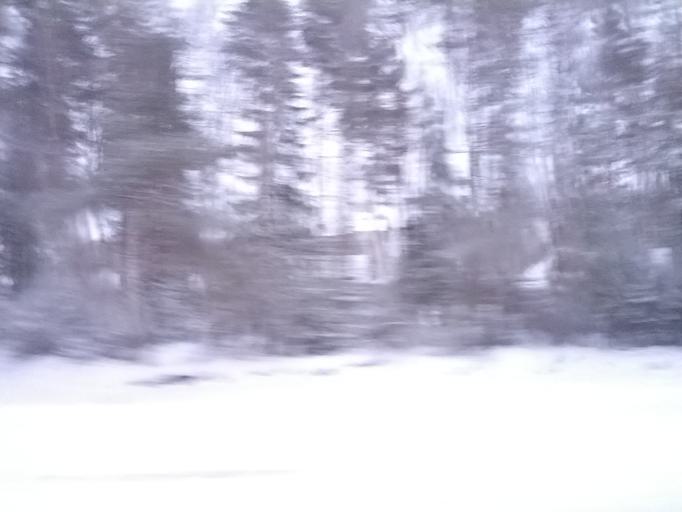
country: RU
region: Mariy-El
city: Suslonger
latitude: 56.3077
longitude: 48.2344
